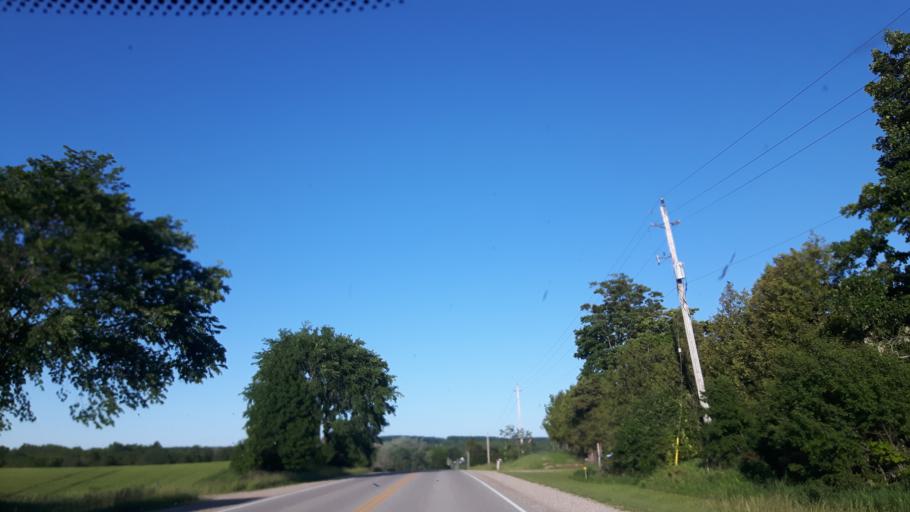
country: CA
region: Ontario
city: Goderich
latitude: 43.6428
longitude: -81.6147
